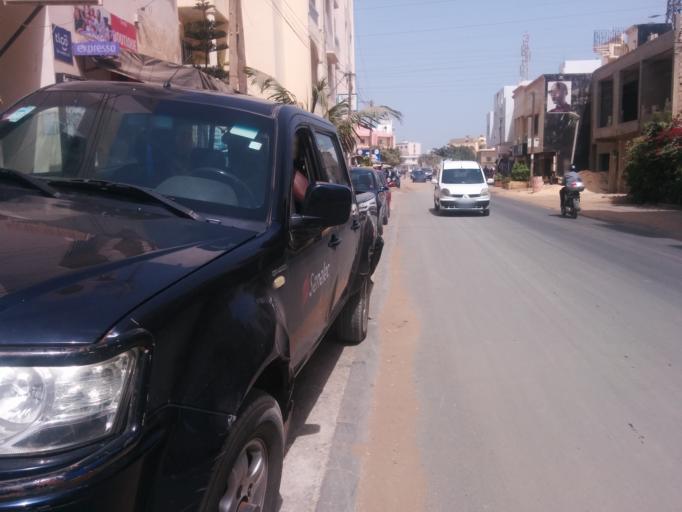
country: SN
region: Dakar
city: Grand Dakar
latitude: 14.7356
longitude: -17.4336
